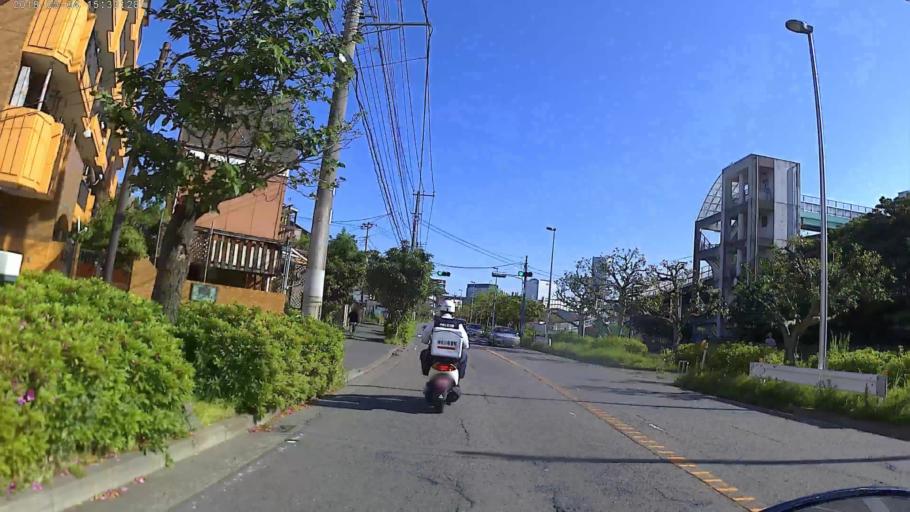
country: JP
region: Kanagawa
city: Yokohama
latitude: 35.5202
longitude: 139.6203
